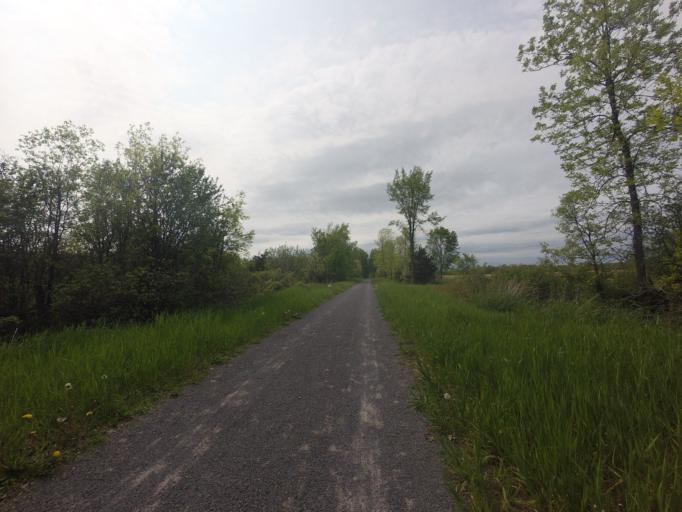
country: CA
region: Ontario
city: Kingston
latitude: 44.3436
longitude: -76.6029
